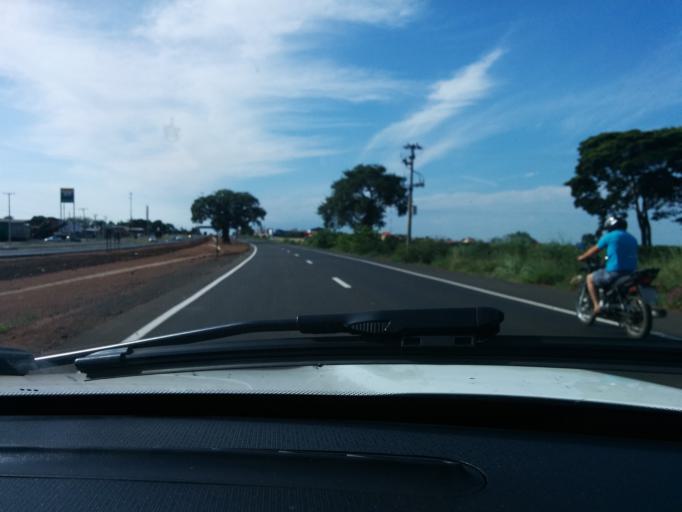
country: BR
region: Sao Paulo
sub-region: Franca
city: Franca
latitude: -20.4656
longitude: -47.4146
